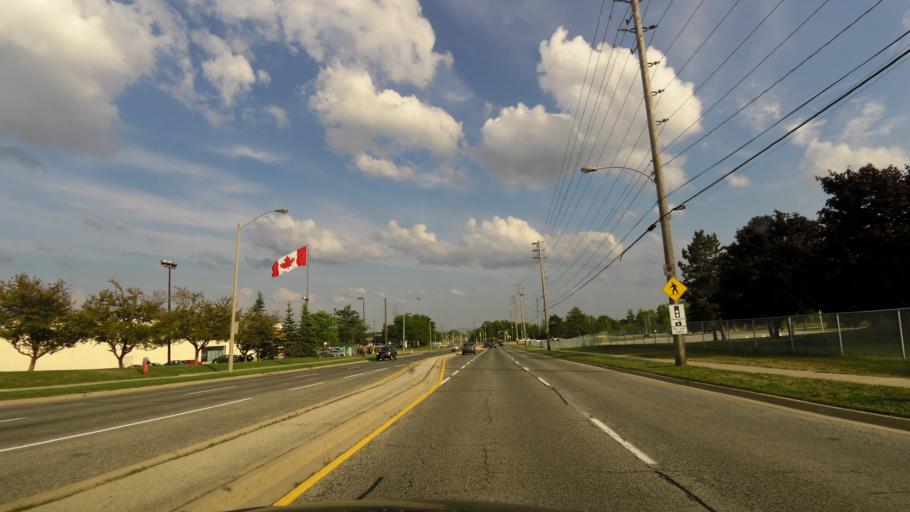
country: CA
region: Ontario
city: Burlington
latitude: 43.3661
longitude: -79.8242
